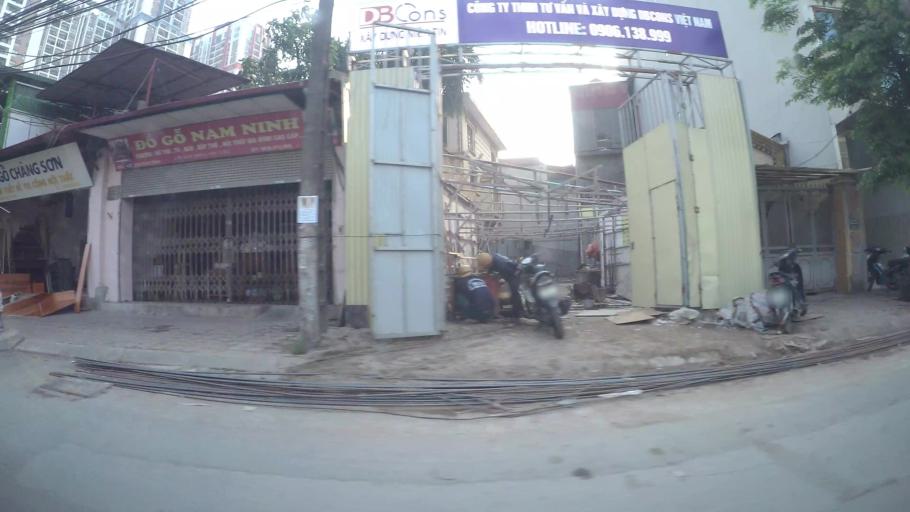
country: VN
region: Ha Noi
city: Thanh Xuan
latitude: 20.9871
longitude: 105.8131
